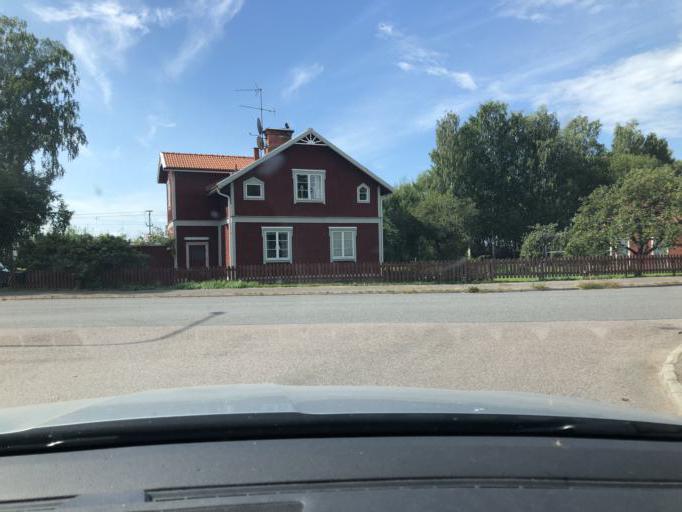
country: SE
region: Dalarna
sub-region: Avesta Kommun
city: Avesta
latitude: 60.1421
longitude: 16.1993
